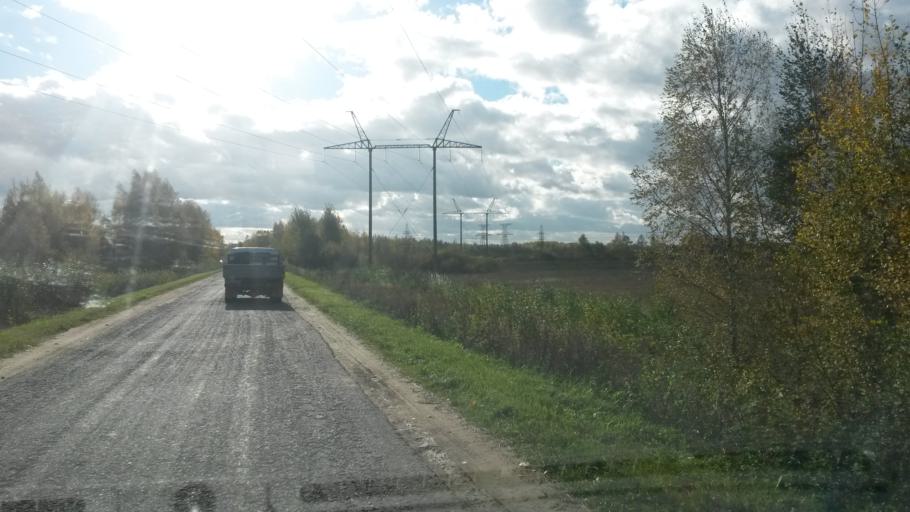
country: RU
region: Jaroslavl
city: Tunoshna
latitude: 57.5351
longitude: 40.0191
